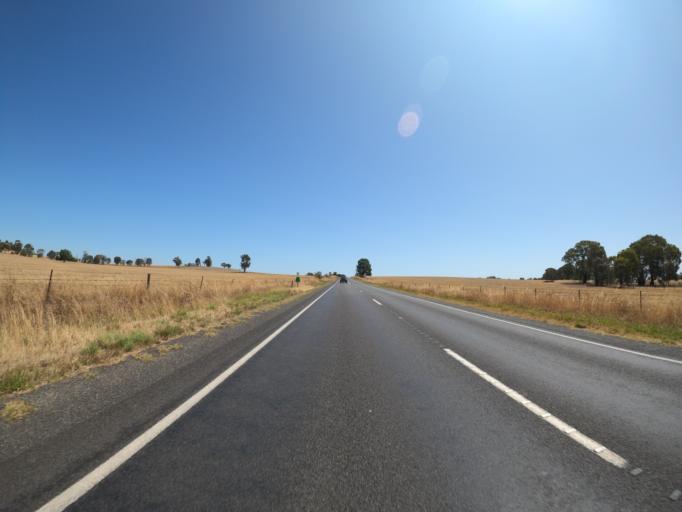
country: AU
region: New South Wales
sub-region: Corowa Shire
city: Corowa
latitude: -36.0551
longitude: 146.4443
